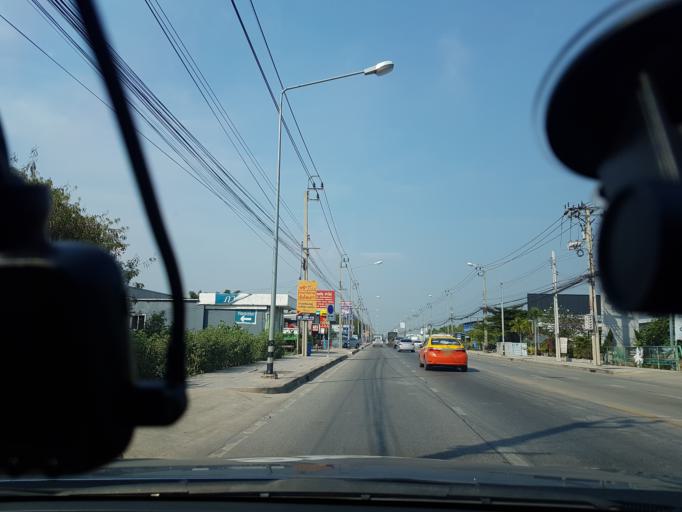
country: TH
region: Pathum Thani
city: Lam Luk Ka
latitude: 13.8879
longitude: 100.7221
